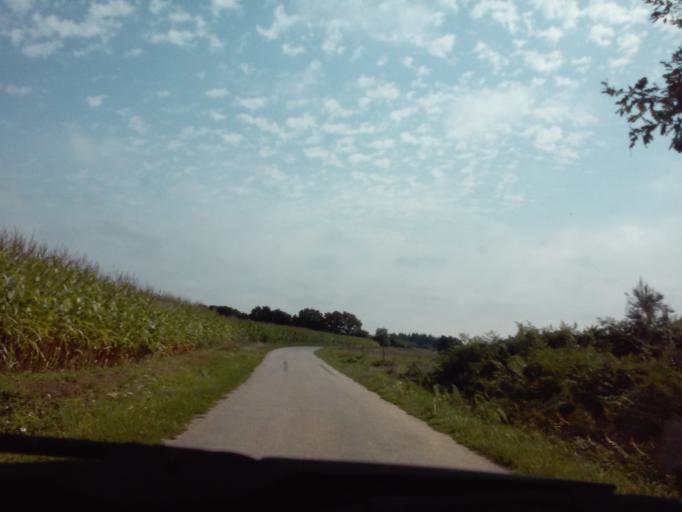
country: FR
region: Brittany
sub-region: Departement du Morbihan
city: Ploermel
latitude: 47.9046
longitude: -2.3978
